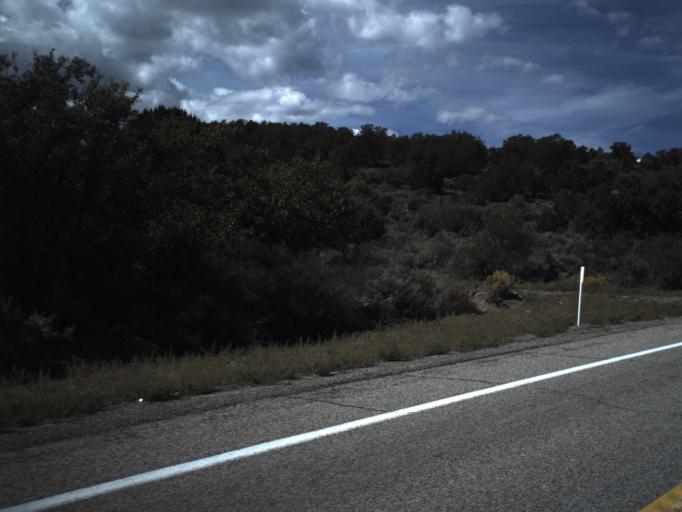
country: US
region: Utah
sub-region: Washington County
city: Enterprise
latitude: 37.4641
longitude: -113.6347
